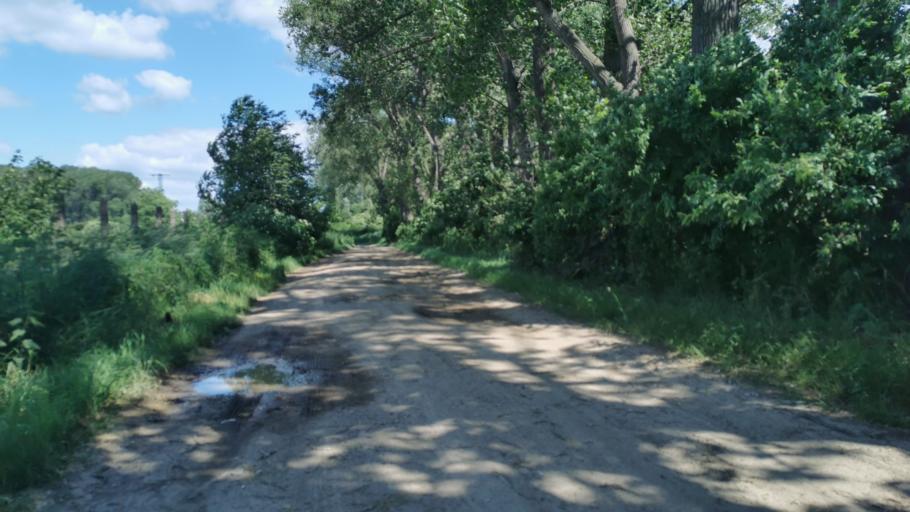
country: SK
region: Trnavsky
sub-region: Okres Skalica
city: Skalica
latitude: 48.8560
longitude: 17.2229
